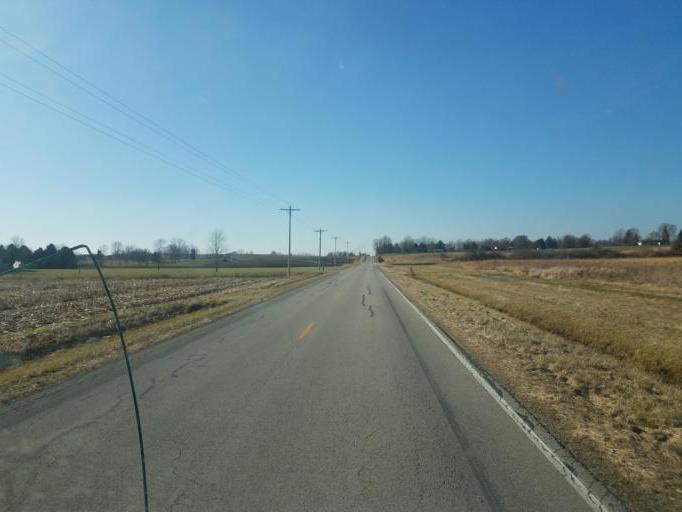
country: US
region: Ohio
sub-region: Marion County
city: Marion
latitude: 40.6443
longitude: -83.1675
